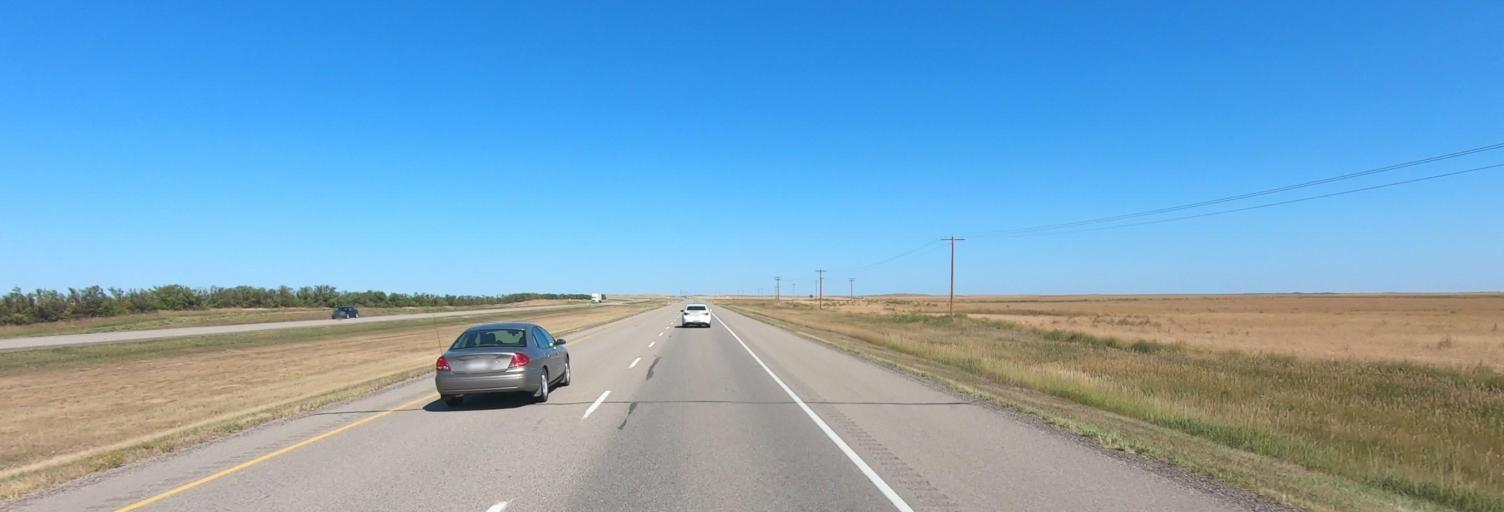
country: CA
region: Alberta
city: Bassano
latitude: 50.8095
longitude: -112.4510
